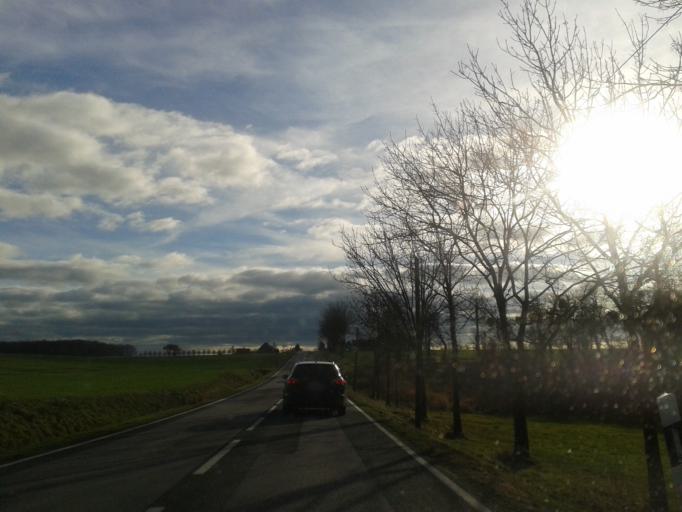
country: DE
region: Saxony
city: Weissenberg
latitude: 51.1729
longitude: 14.6518
